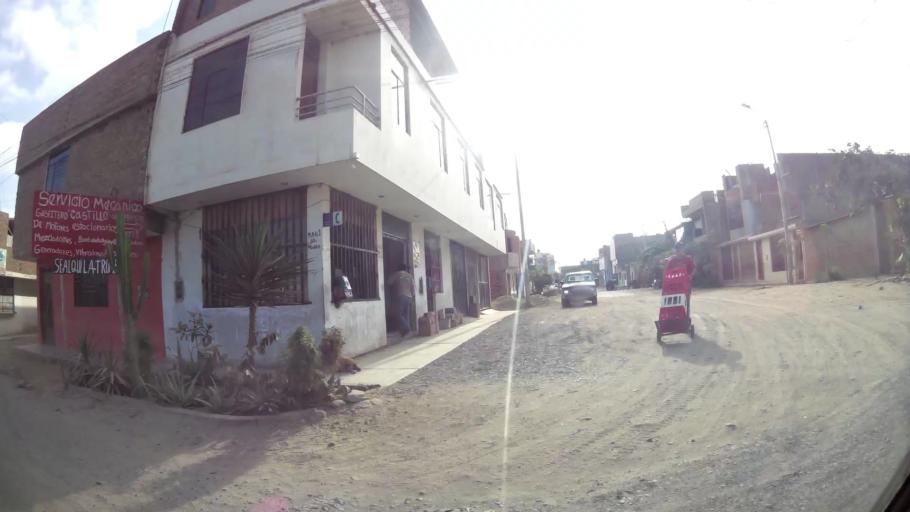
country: PE
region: La Libertad
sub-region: Provincia de Trujillo
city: La Esperanza
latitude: -8.0881
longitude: -79.0361
